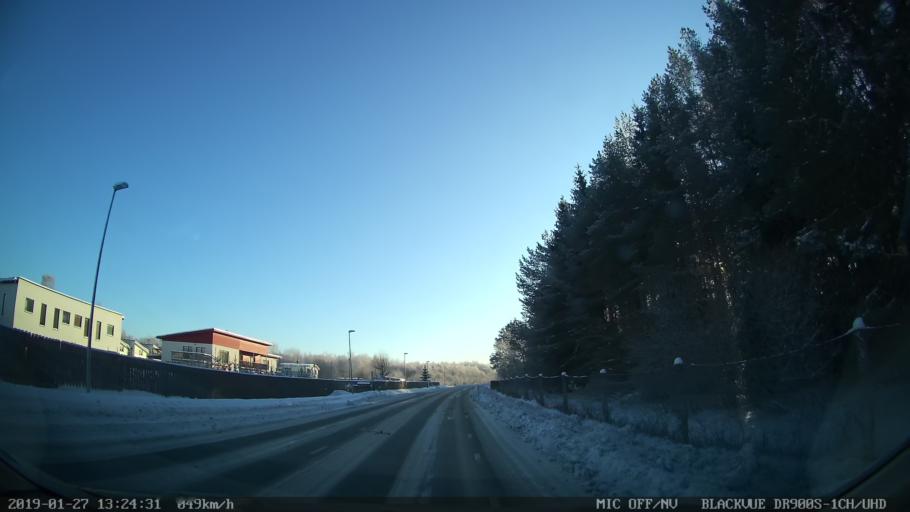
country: EE
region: Harju
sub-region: Tallinna linn
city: Tallinn
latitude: 59.3991
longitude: 24.7918
